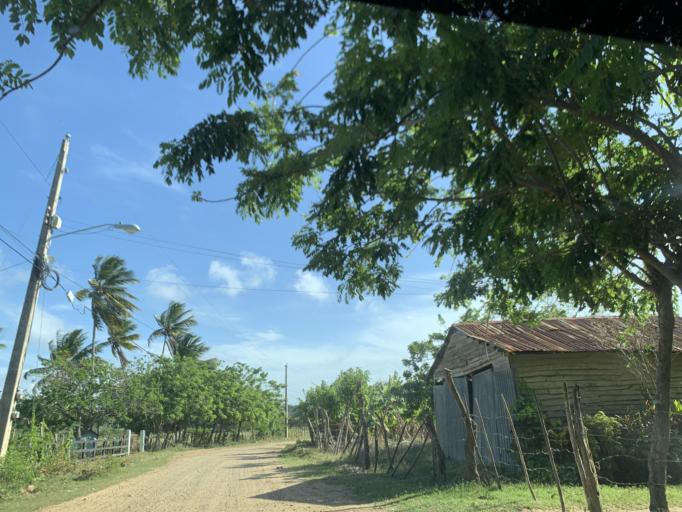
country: DO
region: Puerto Plata
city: Luperon
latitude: 19.8956
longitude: -70.8807
